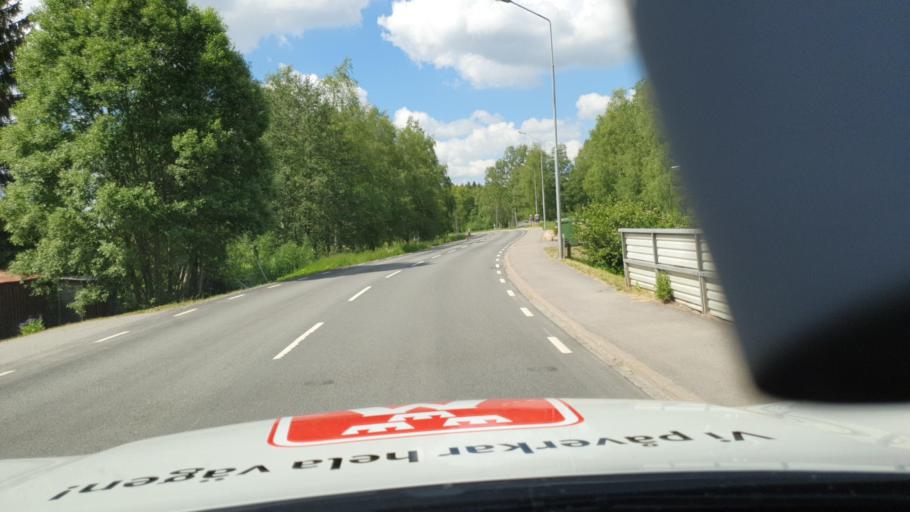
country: SE
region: Joenkoeping
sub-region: Mullsjo Kommun
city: Mullsjoe
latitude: 57.9878
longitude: 13.7686
